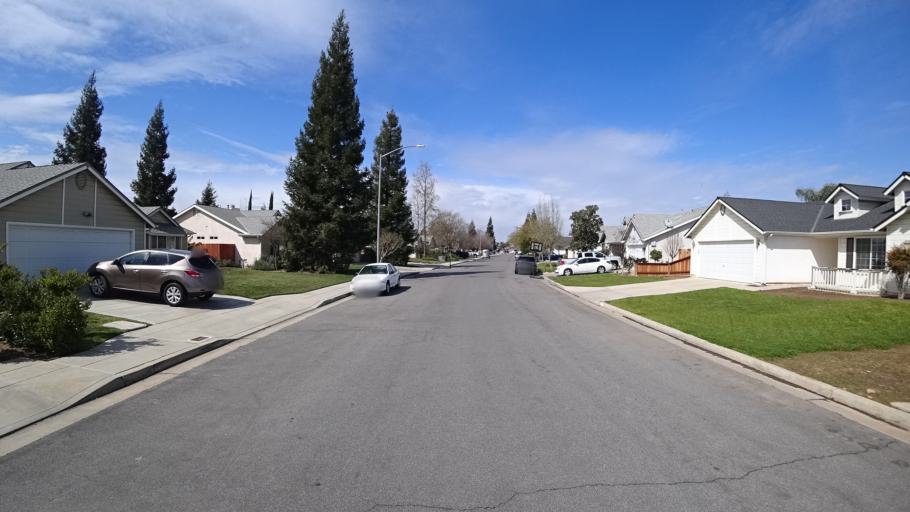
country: US
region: California
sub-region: Fresno County
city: Biola
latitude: 36.8491
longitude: -119.8942
